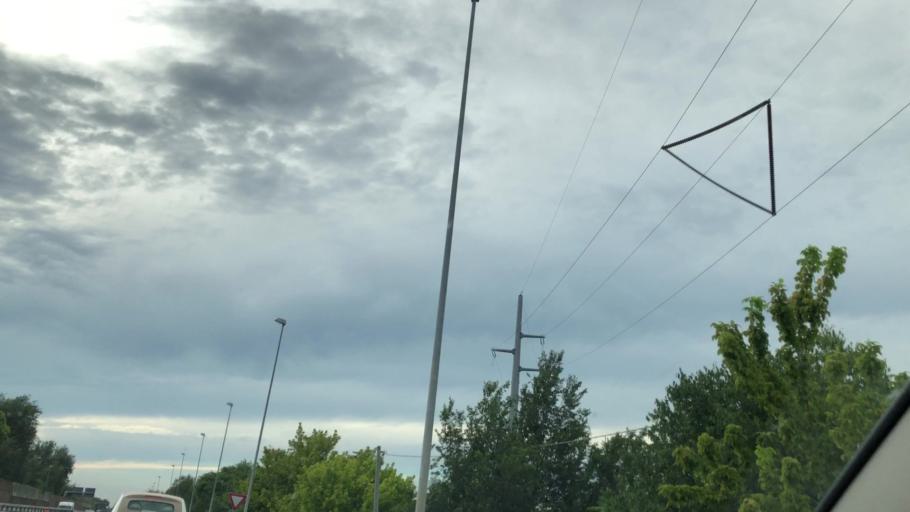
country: IT
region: Emilia-Romagna
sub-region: Provincia di Bologna
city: Calderara di Reno
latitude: 44.5209
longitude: 11.2795
